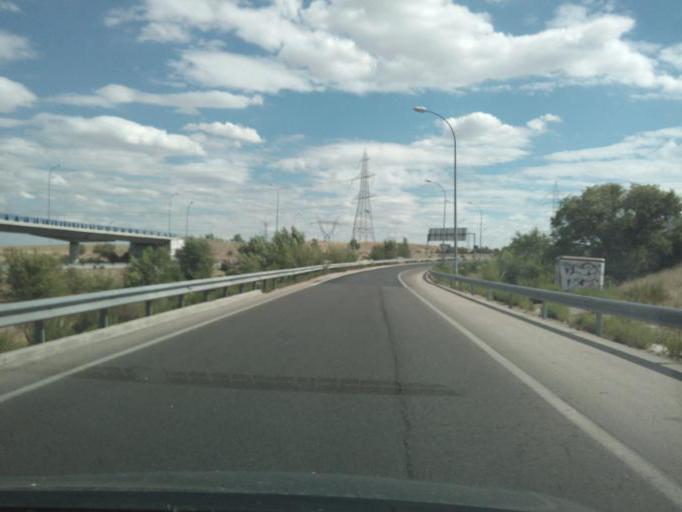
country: ES
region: Madrid
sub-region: Provincia de Madrid
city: San Sebastian de los Reyes
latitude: 40.5536
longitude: -3.6080
